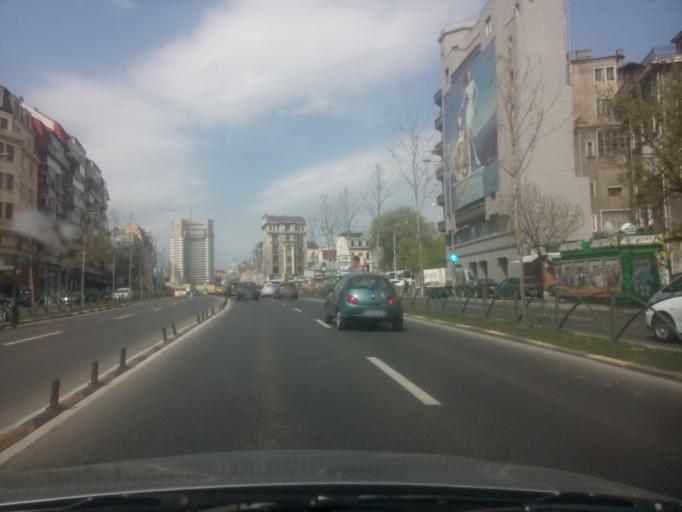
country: RO
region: Bucuresti
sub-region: Municipiul Bucuresti
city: Bucharest
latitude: 44.4313
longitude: 26.1037
